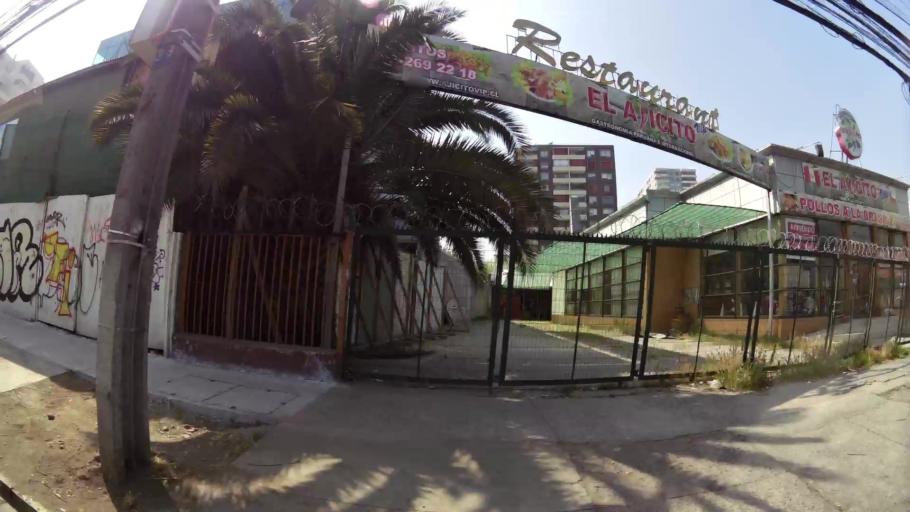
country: CL
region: Santiago Metropolitan
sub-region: Provincia de Santiago
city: Villa Presidente Frei, Nunoa, Santiago, Chile
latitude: -33.4535
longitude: -70.6001
